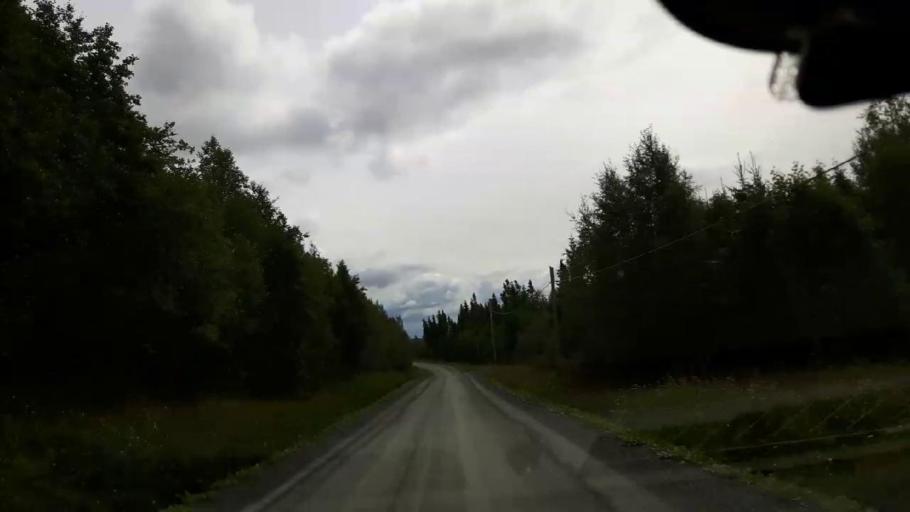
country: SE
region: Jaemtland
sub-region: Krokoms Kommun
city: Valla
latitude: 63.6815
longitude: 13.9234
